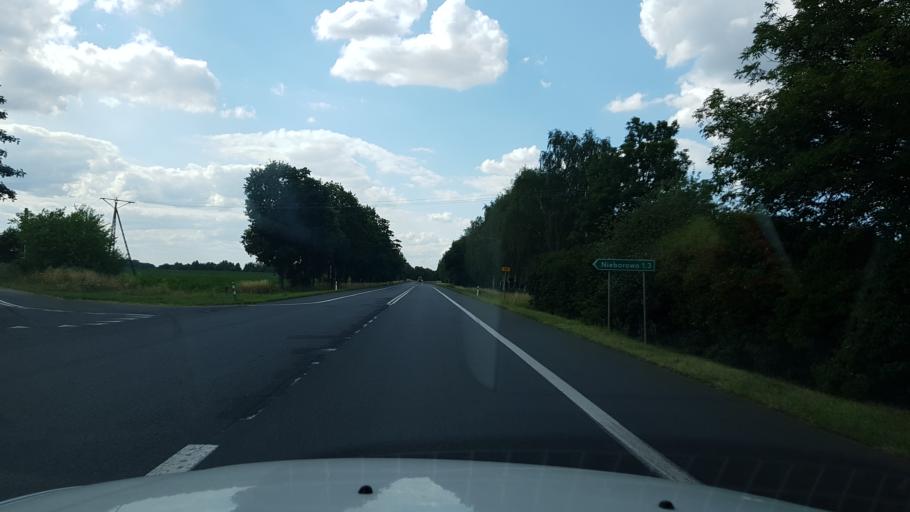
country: PL
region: West Pomeranian Voivodeship
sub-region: Powiat pyrzycki
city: Pyrzyce
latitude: 53.1970
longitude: 14.8263
